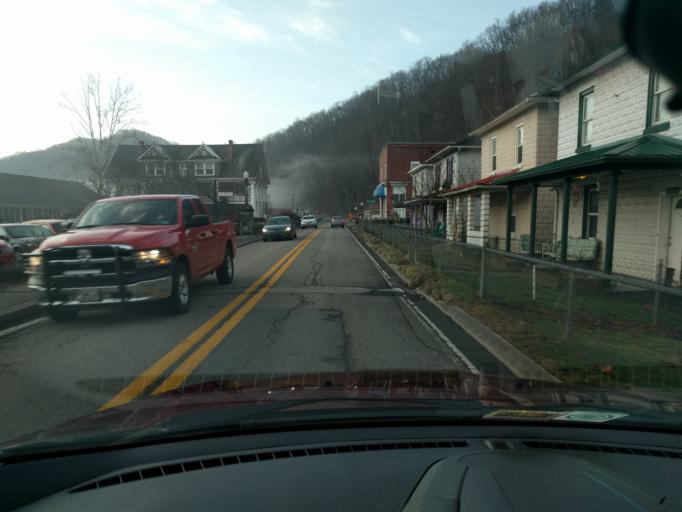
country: US
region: West Virginia
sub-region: Fayette County
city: Ansted
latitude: 38.1510
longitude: -81.2150
